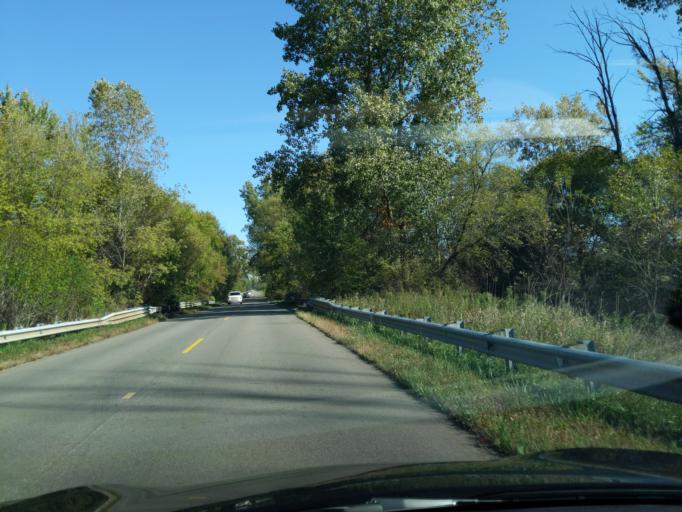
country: US
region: Michigan
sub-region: Eaton County
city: Potterville
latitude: 42.6403
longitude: -84.7704
